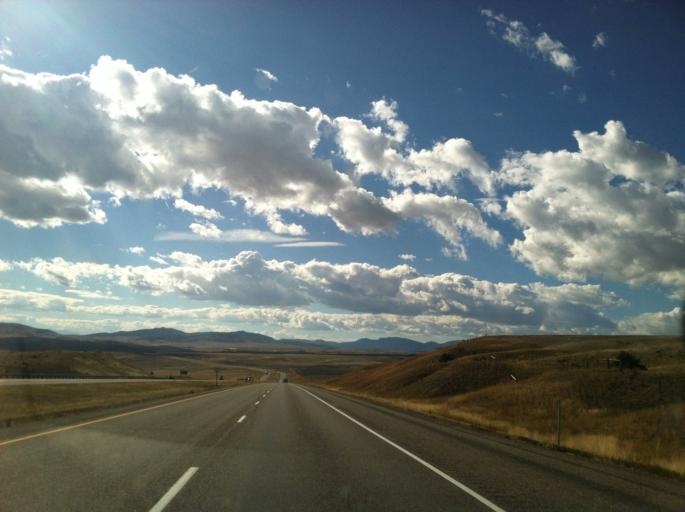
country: US
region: Montana
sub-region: Gallatin County
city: Three Forks
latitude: 45.9198
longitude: -111.6824
